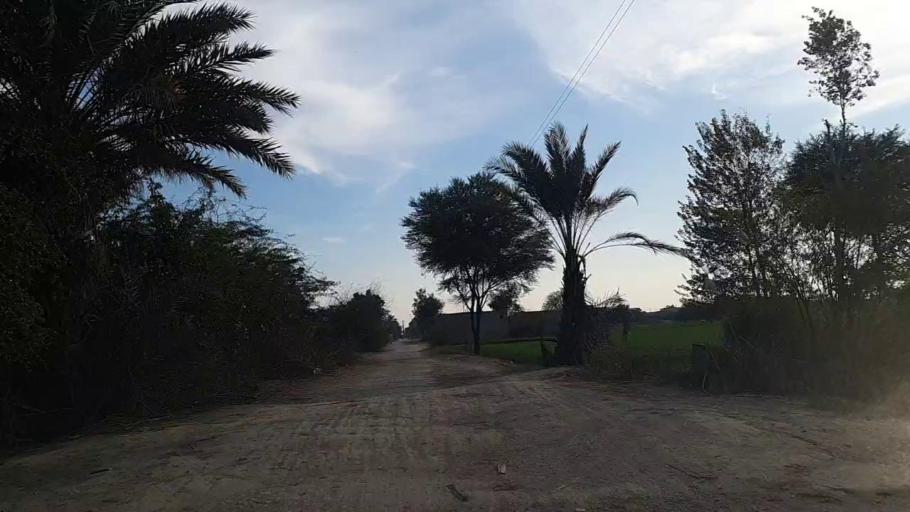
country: PK
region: Sindh
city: Bandhi
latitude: 26.5644
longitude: 68.2786
